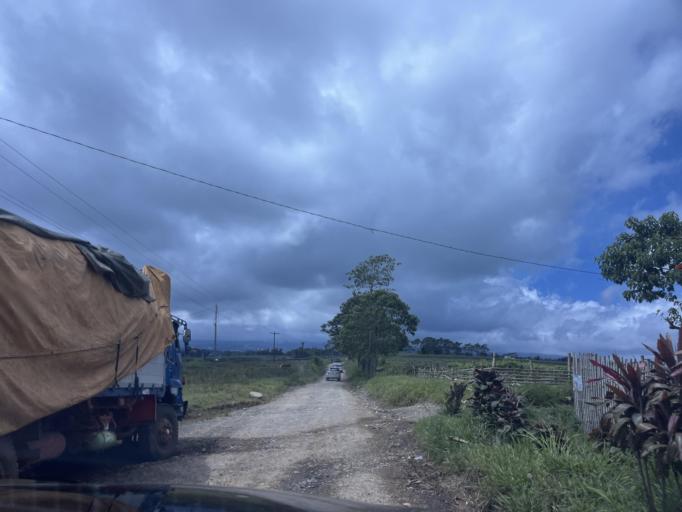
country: PH
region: Northern Mindanao
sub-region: Province of Bukidnon
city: Impalutao
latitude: 8.2204
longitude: 124.9946
